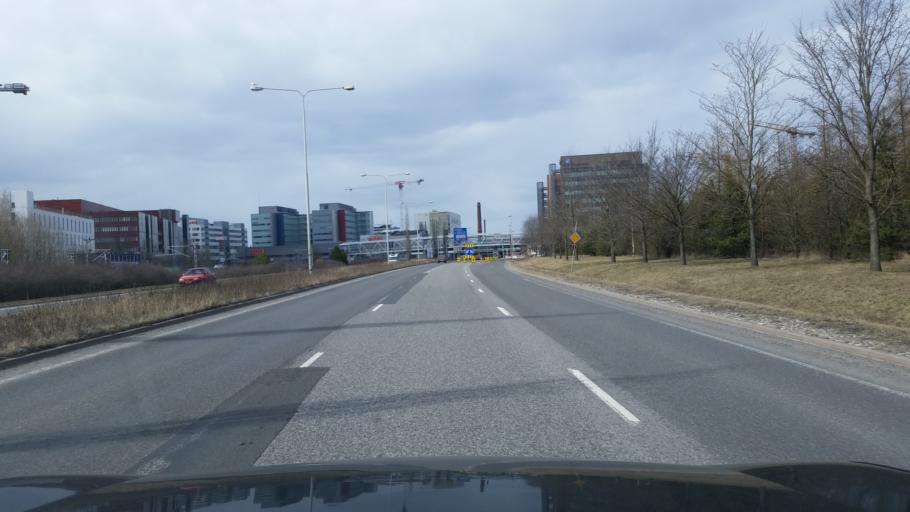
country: FI
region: Varsinais-Suomi
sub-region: Turku
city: Turku
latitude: 60.4476
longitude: 22.3025
